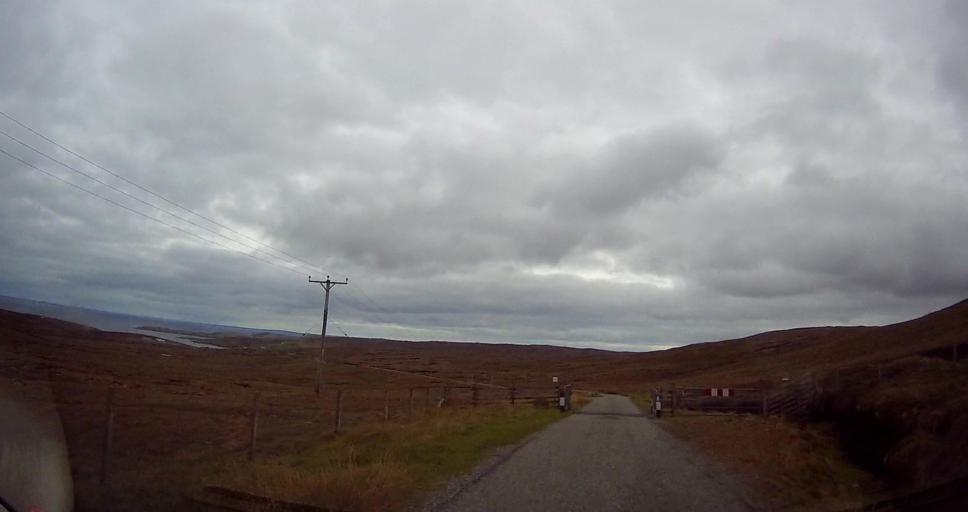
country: GB
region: Scotland
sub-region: Shetland Islands
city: Shetland
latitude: 60.5703
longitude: -1.0669
